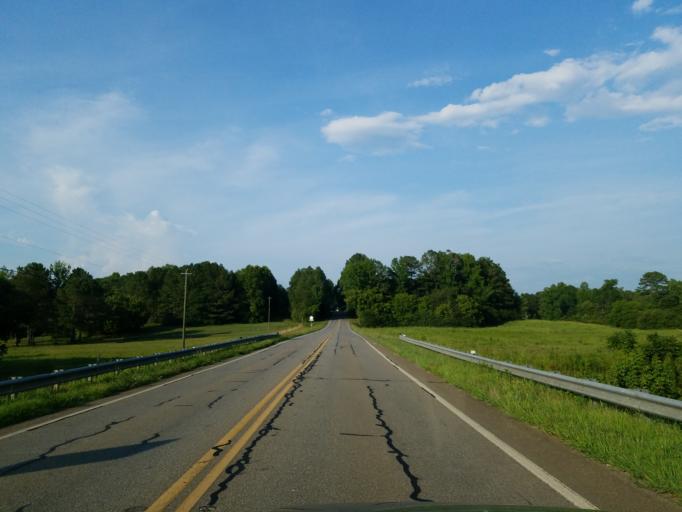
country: US
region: Georgia
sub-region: Pickens County
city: Jasper
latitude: 34.4995
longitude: -84.5682
